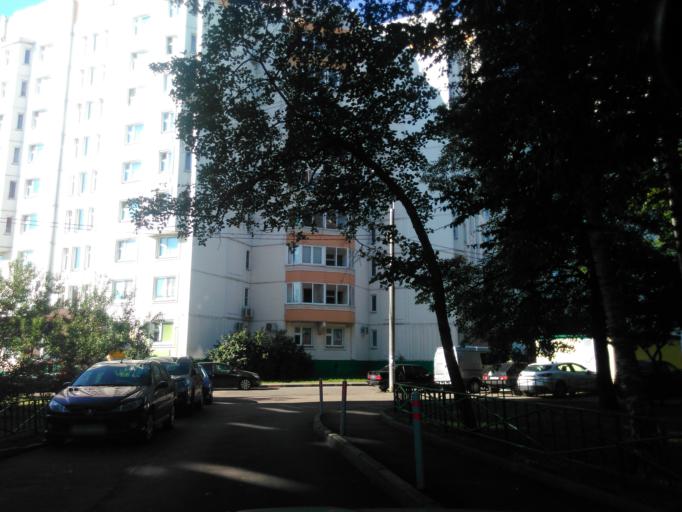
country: RU
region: Moscow
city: Zapadnoye Degunino
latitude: 55.8684
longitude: 37.5364
